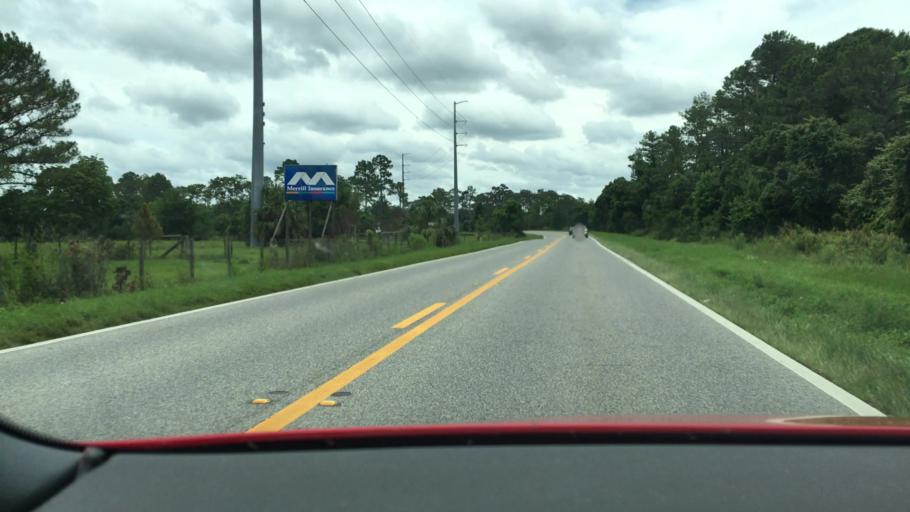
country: US
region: Florida
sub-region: Lake County
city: Eustis
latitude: 28.8711
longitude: -81.6632
